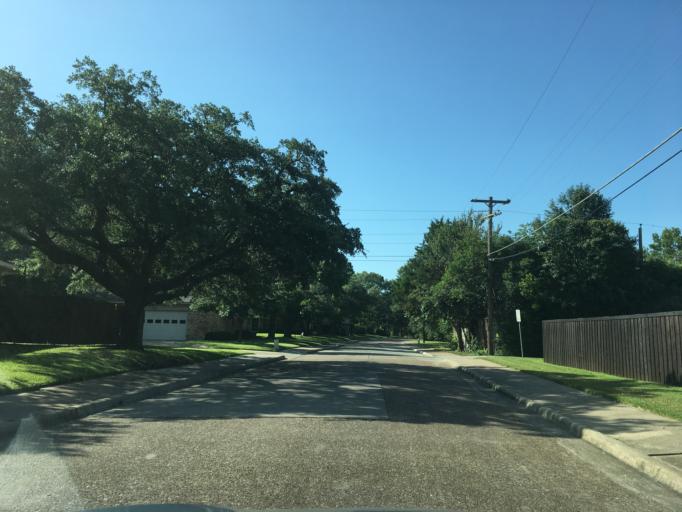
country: US
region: Texas
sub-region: Dallas County
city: Richardson
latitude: 32.8822
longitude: -96.7247
